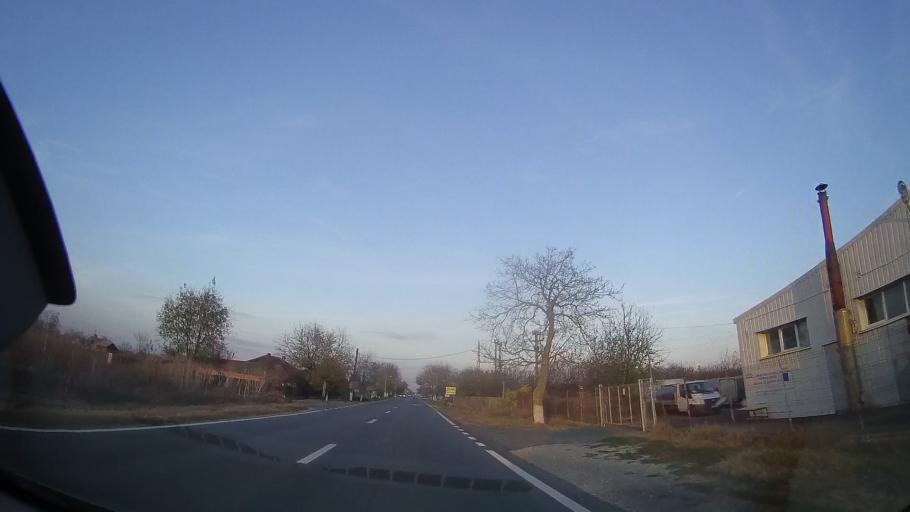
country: RO
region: Constanta
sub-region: Comuna Topraisar
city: Topraisar
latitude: 44.0072
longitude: 28.4433
